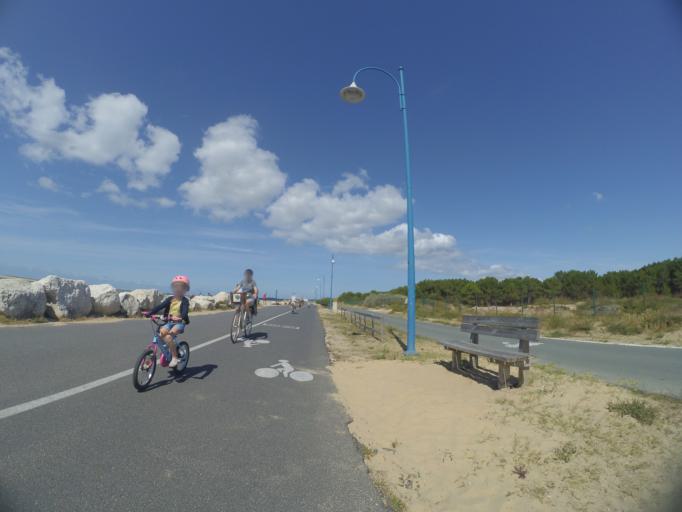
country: FR
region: Poitou-Charentes
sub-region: Departement de la Charente-Maritime
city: Les Mathes
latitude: 45.6790
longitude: -1.1740
